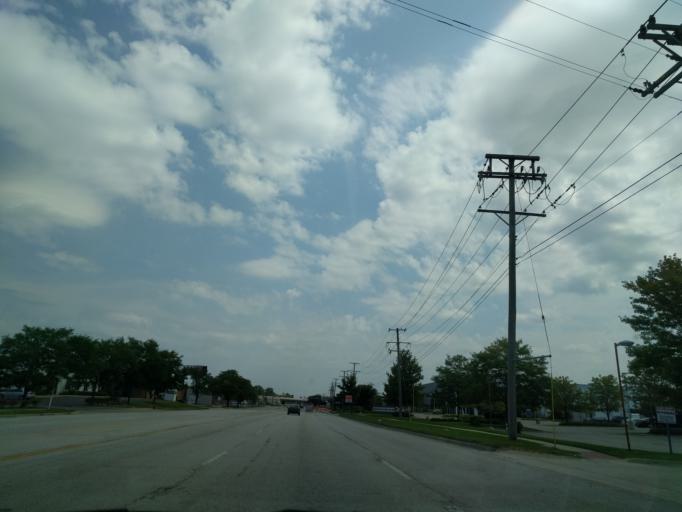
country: US
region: Illinois
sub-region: Cook County
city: Rosemont
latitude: 42.0086
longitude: -87.9135
